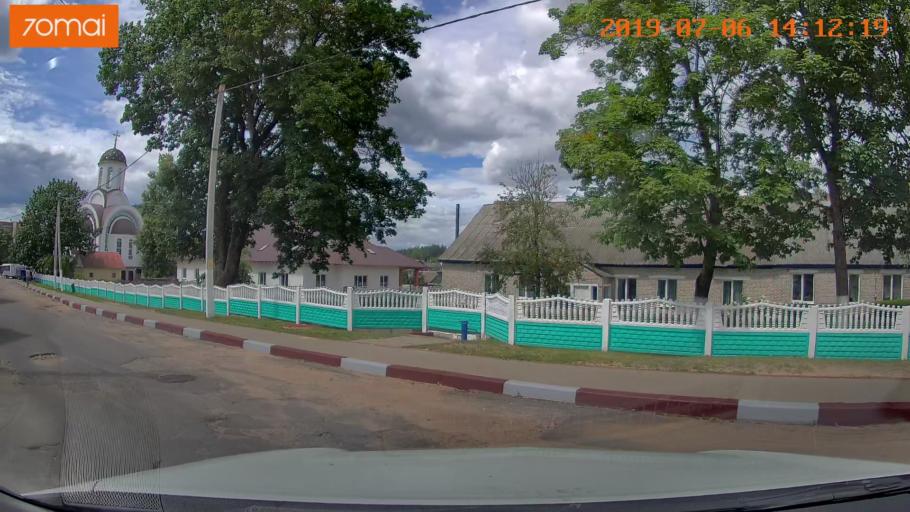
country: BY
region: Minsk
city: Ivyanyets
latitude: 53.8892
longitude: 26.7433
